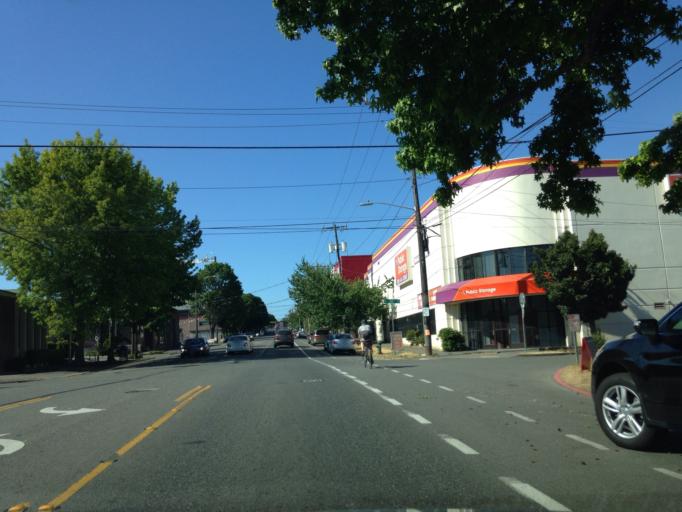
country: US
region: Washington
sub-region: King County
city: Seattle
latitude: 47.6503
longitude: -122.3427
